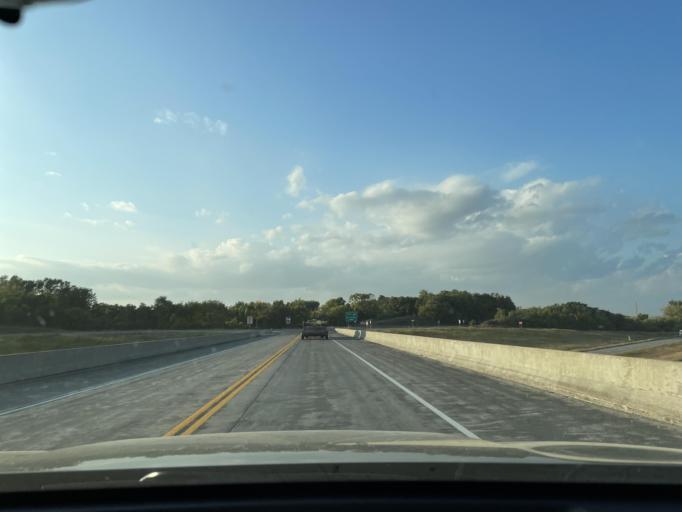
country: US
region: Missouri
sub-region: Andrew County
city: Country Club Village
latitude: 39.8351
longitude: -94.8647
